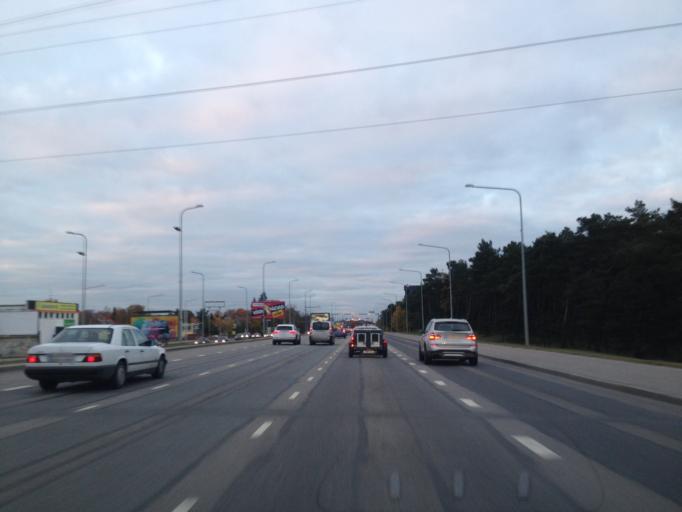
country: EE
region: Harju
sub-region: Tallinna linn
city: Tallinn
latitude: 59.3964
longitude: 24.7262
